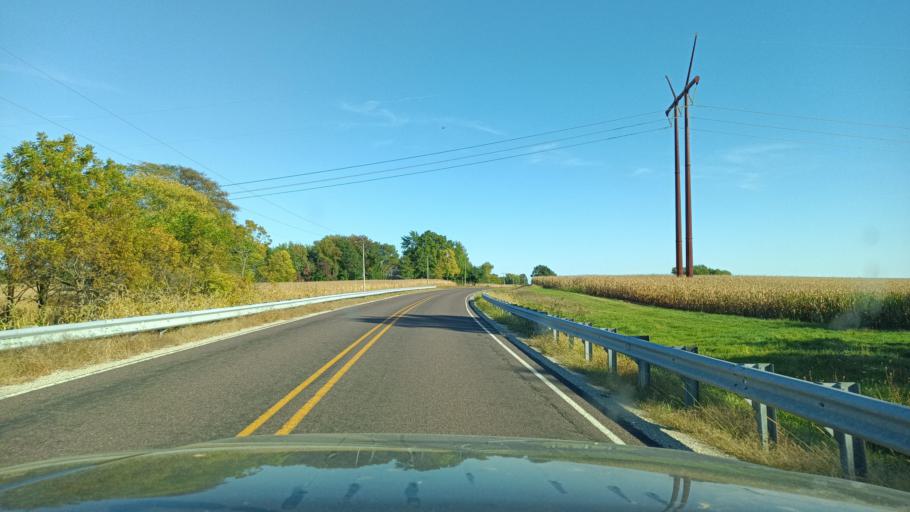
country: US
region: Illinois
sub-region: McLean County
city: Heyworth
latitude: 40.2379
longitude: -89.0795
